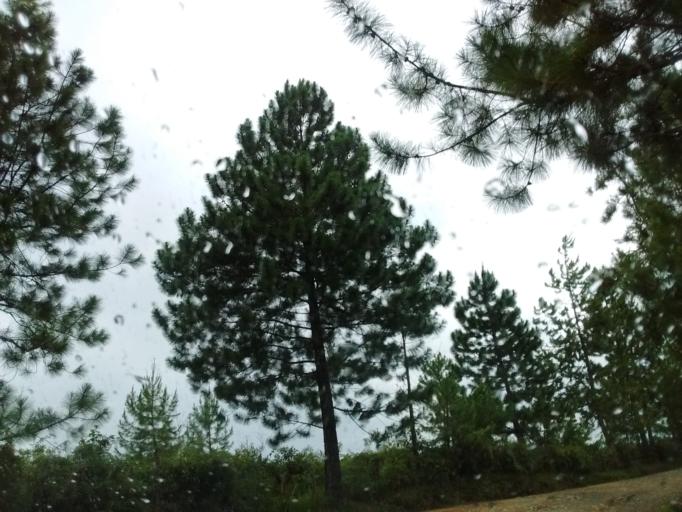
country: CO
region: Cauca
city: Cajibio
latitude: 2.5733
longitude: -76.6471
